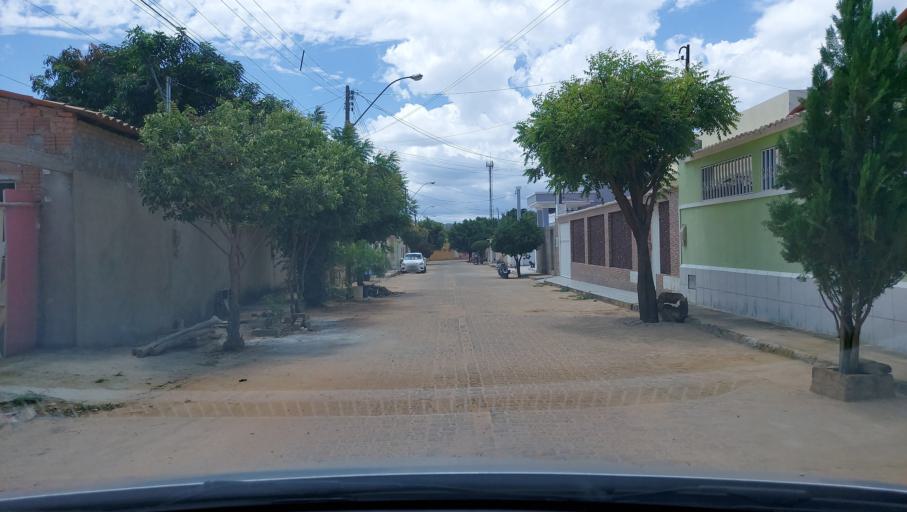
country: BR
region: Bahia
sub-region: Oliveira Dos Brejinhos
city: Beira Rio
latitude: -12.0017
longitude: -42.6283
